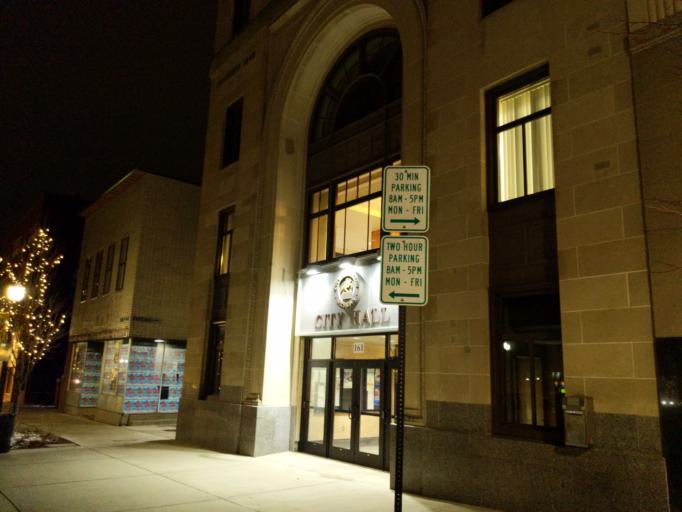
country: US
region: Michigan
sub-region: Jackson County
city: Jackson
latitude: 42.2475
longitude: -84.4084
